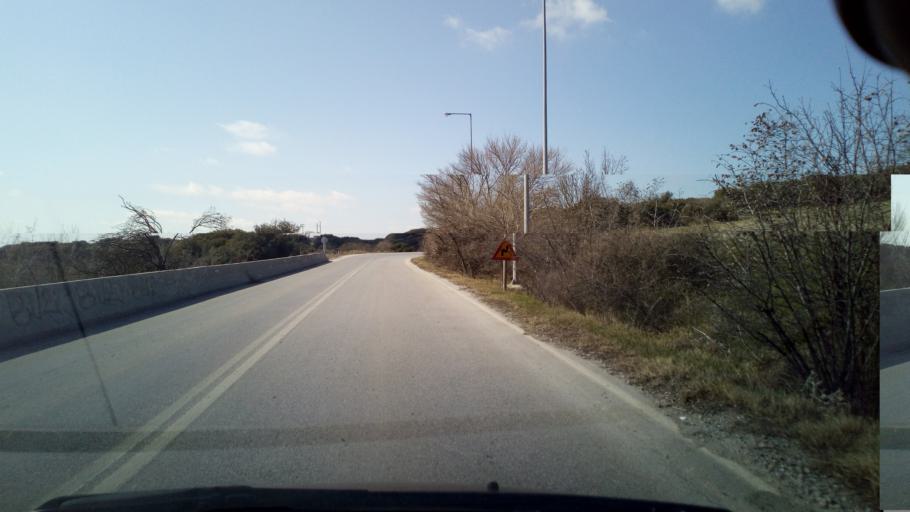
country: GR
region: Central Macedonia
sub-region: Nomos Thessalonikis
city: Chortiatis
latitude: 40.6186
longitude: 23.0640
